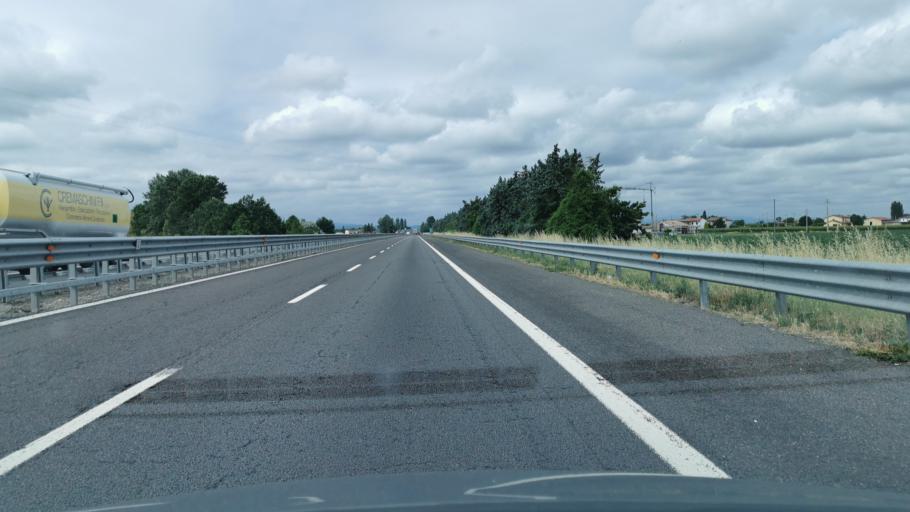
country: IT
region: Emilia-Romagna
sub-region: Provincia di Ravenna
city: Barbiano
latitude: 44.3781
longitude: 11.8789
